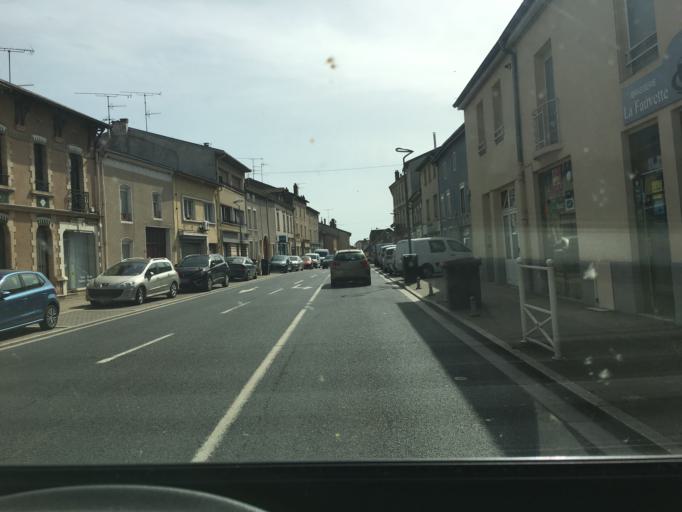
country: FR
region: Lorraine
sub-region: Departement de Meurthe-et-Moselle
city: Neuves-Maisons
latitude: 48.6163
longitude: 6.1053
